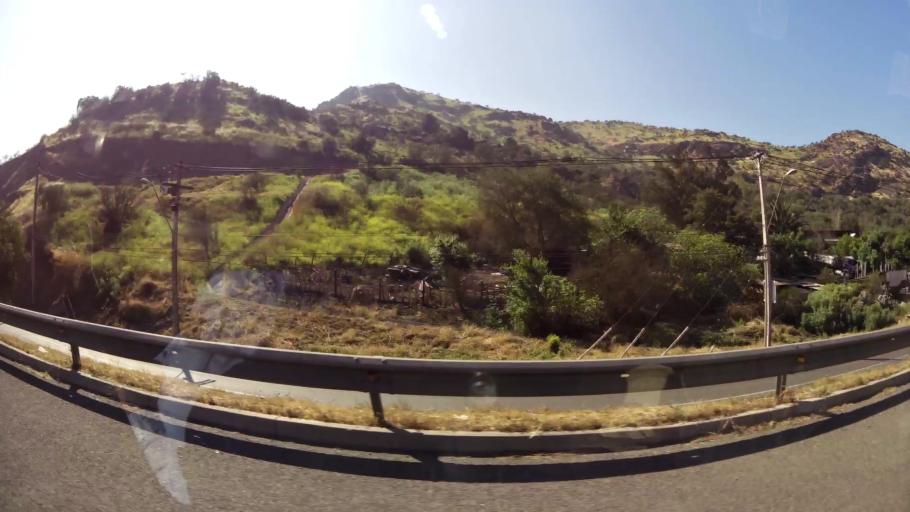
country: CL
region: Santiago Metropolitan
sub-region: Provincia de Chacabuco
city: Chicureo Abajo
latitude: -33.3441
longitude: -70.6942
